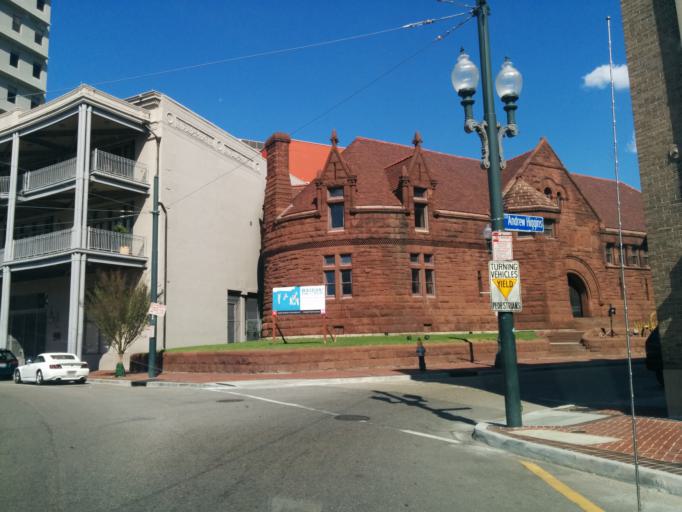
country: US
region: Louisiana
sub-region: Orleans Parish
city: New Orleans
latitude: 29.9431
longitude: -90.0720
